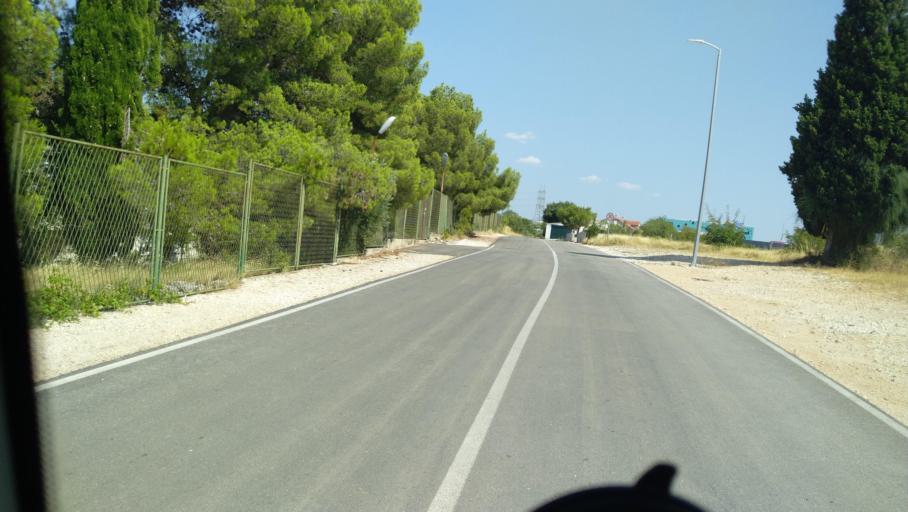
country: HR
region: Sibensko-Kniniska
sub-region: Grad Sibenik
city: Sibenik
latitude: 43.7161
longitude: 15.9089
